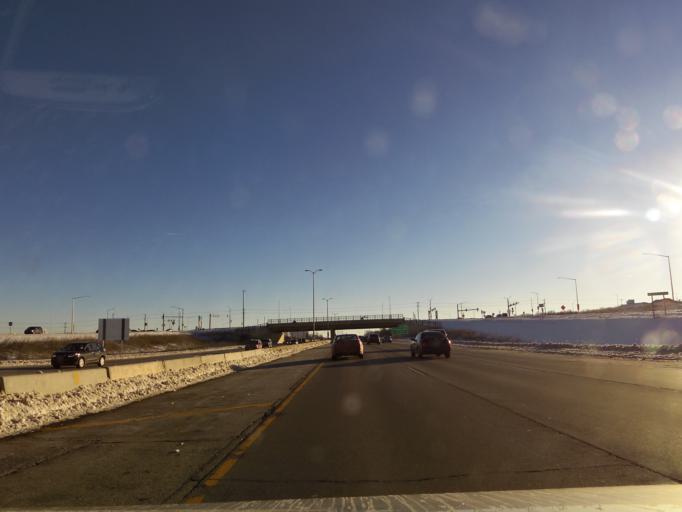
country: US
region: Wisconsin
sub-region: Milwaukee County
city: Greendale
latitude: 42.9184
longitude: -87.9355
